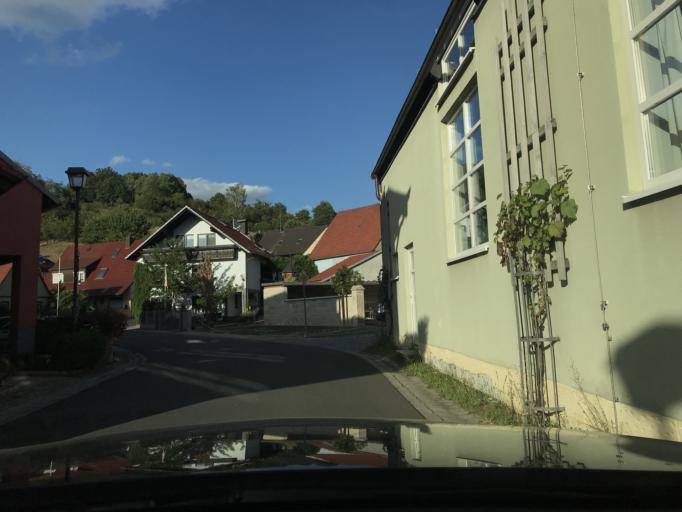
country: DE
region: Bavaria
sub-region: Regierungsbezirk Unterfranken
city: Breitbrunn
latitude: 50.0367
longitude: 10.6909
